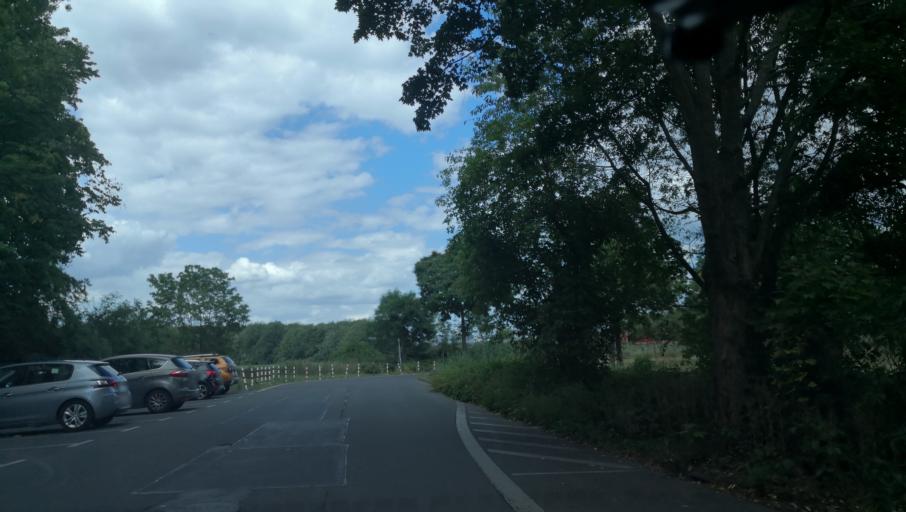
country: DE
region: North Rhine-Westphalia
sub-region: Regierungsbezirk Koln
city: Mengenich
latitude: 50.9715
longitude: 6.8867
